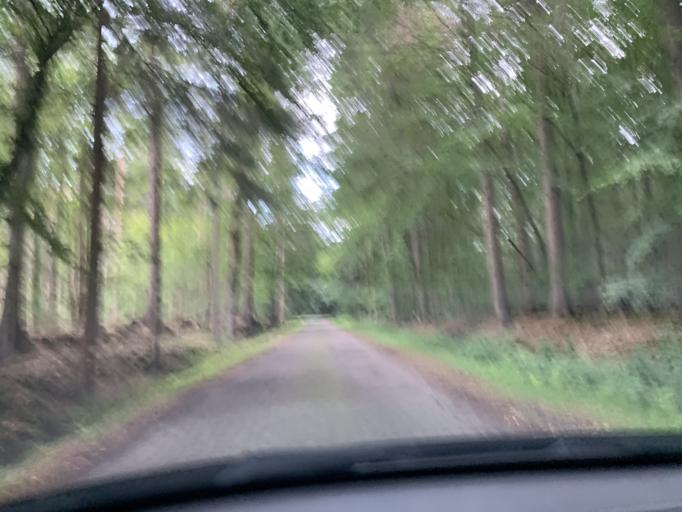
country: DE
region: Lower Saxony
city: Westerstede
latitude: 53.2689
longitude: 7.9866
